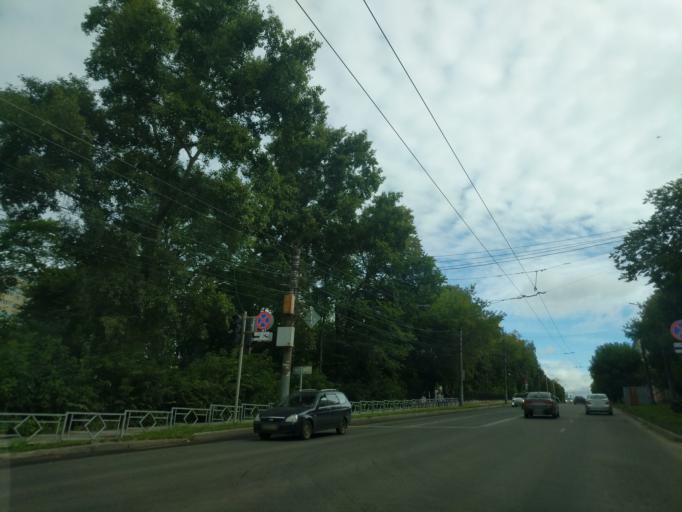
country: RU
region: Kirov
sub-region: Kirovo-Chepetskiy Rayon
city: Kirov
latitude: 58.6033
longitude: 49.6501
